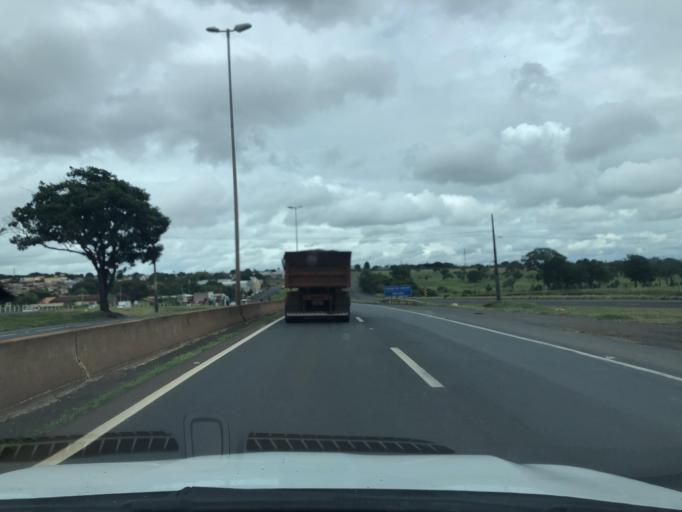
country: BR
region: Minas Gerais
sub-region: Uberaba
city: Uberaba
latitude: -19.7793
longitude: -47.9579
